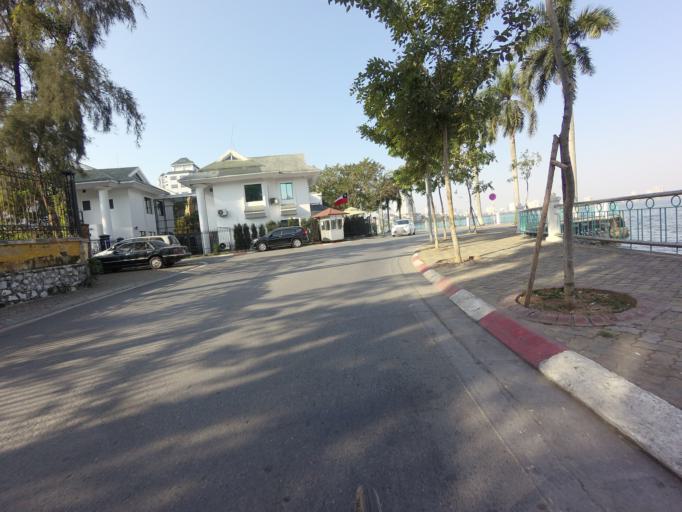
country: VN
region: Ha Noi
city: Hanoi
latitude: 21.0432
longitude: 105.8303
